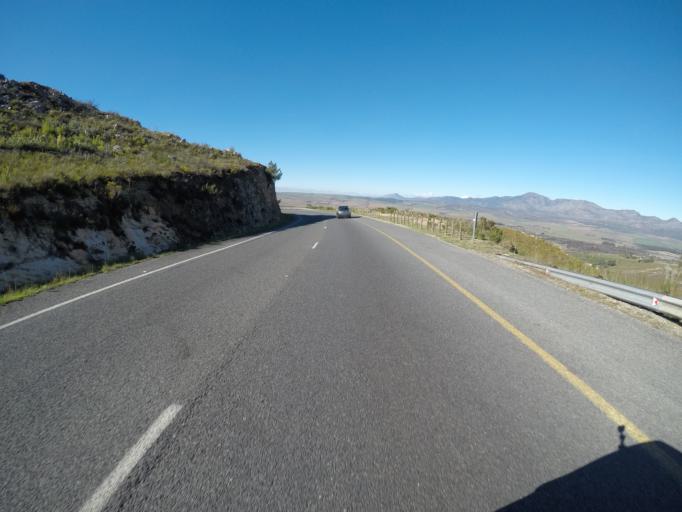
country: ZA
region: Western Cape
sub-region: Overberg District Municipality
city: Grabouw
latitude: -34.2223
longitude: 19.1803
